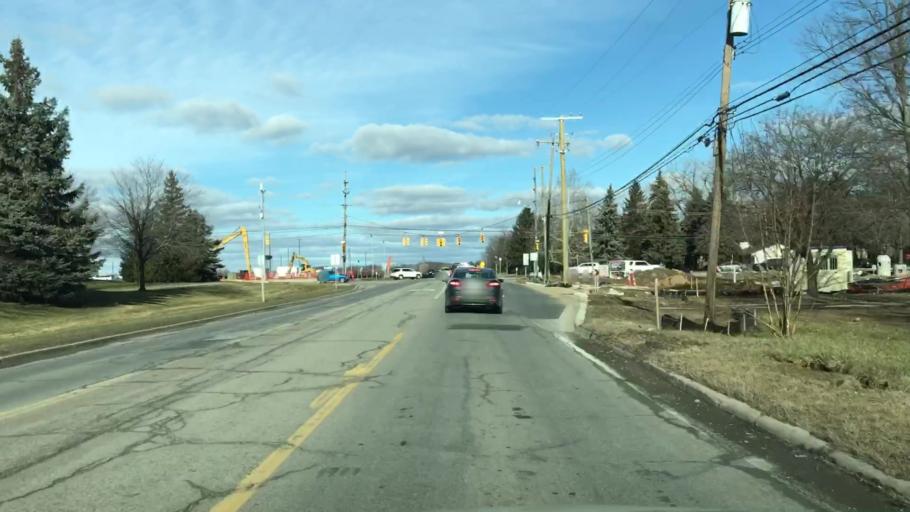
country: US
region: Michigan
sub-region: Oakland County
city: Auburn Hills
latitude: 42.6932
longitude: -83.1945
